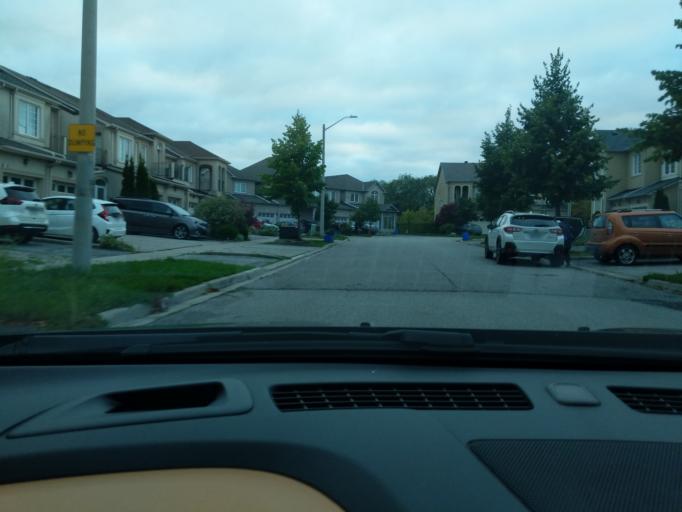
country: CA
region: Ontario
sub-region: York
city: Richmond Hill
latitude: 43.8918
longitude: -79.4128
